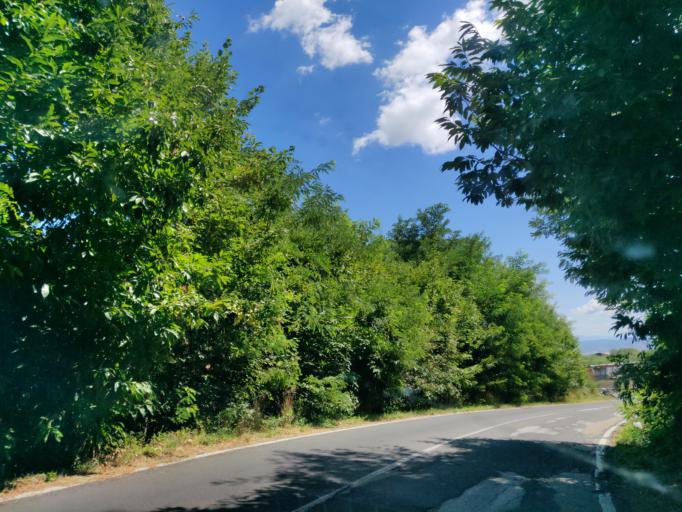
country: IT
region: Tuscany
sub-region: Provincia di Siena
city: Abbadia San Salvatore
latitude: 42.8841
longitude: 11.6609
